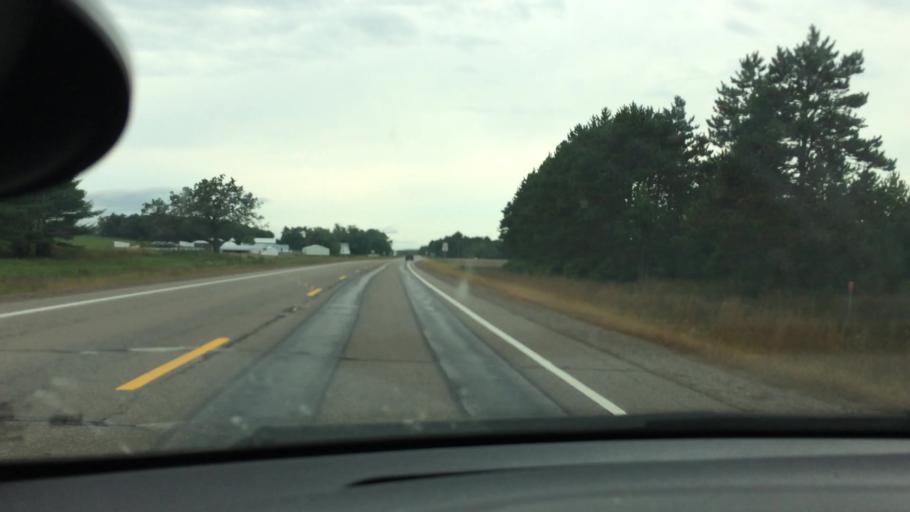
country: US
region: Wisconsin
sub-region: Eau Claire County
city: Augusta
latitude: 44.5848
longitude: -91.1133
